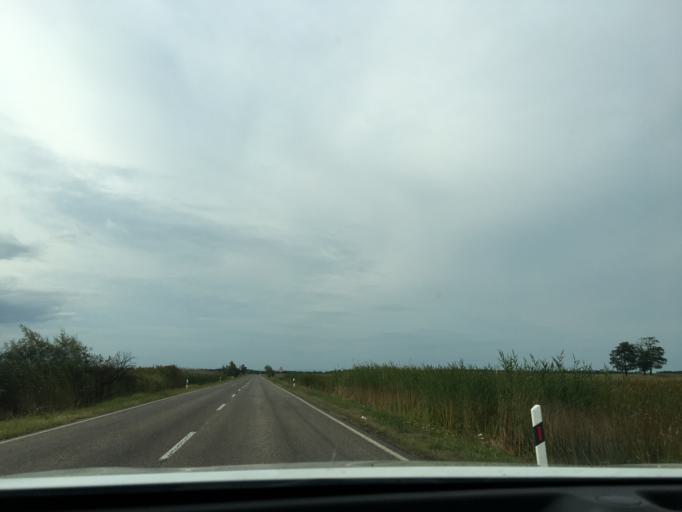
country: HU
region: Hajdu-Bihar
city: Egyek
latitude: 47.5718
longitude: 20.8593
